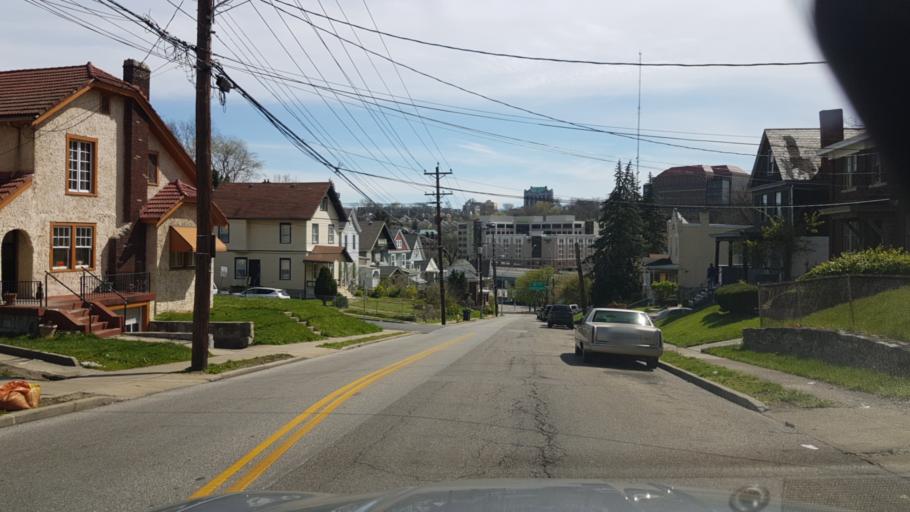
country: US
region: Kentucky
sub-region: Campbell County
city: Bellevue
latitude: 39.1179
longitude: -84.5035
